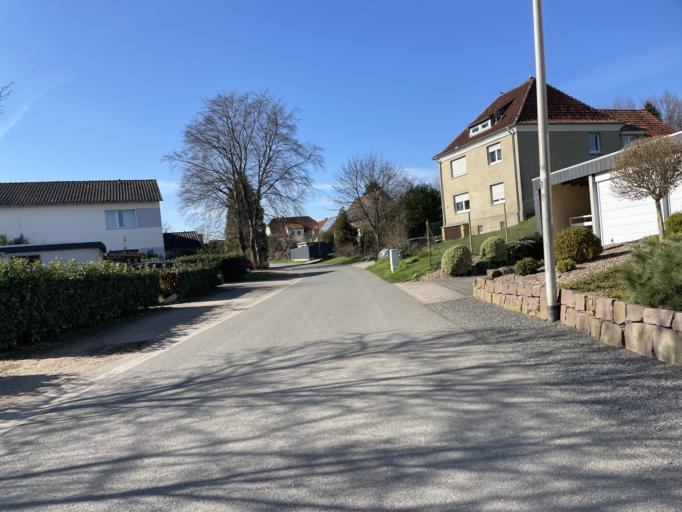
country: DE
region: North Rhine-Westphalia
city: Porta Westfalica
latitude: 52.2343
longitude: 8.9364
